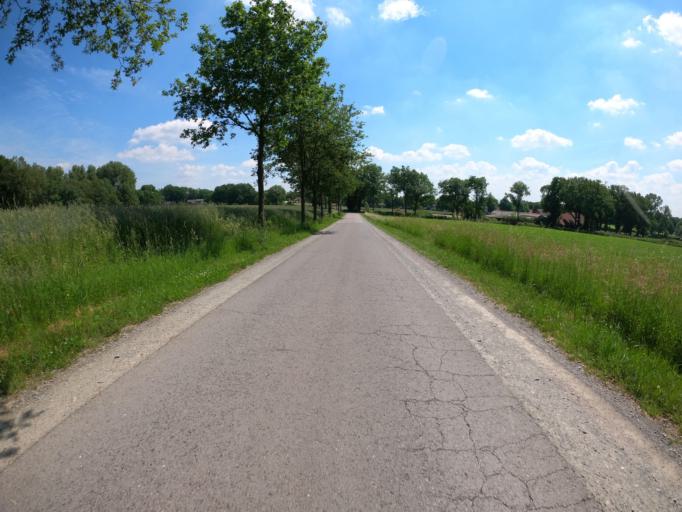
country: DE
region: North Rhine-Westphalia
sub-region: Regierungsbezirk Dusseldorf
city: Schermbeck
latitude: 51.6877
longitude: 6.8509
